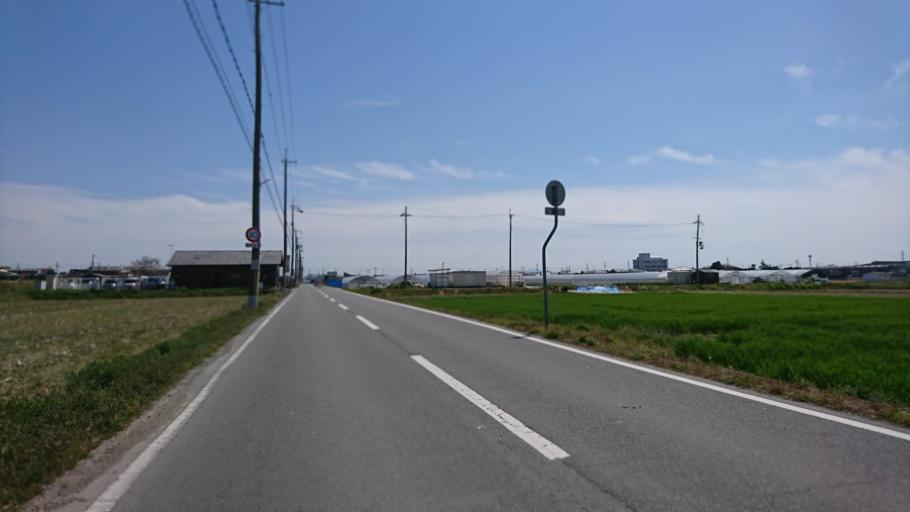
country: JP
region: Hyogo
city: Kakogawacho-honmachi
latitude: 34.7483
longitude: 134.8883
